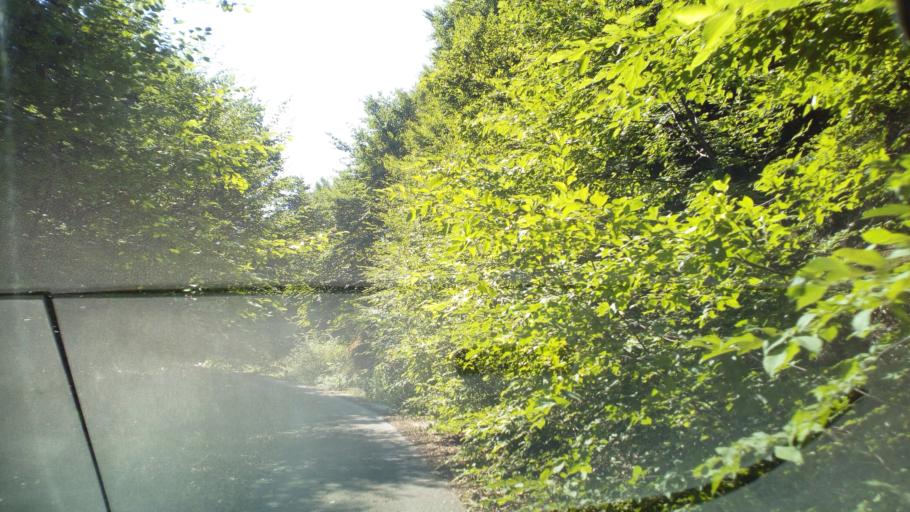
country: GR
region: Central Macedonia
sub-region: Nomos Thessalonikis
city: Sochos
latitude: 40.8271
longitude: 23.3564
